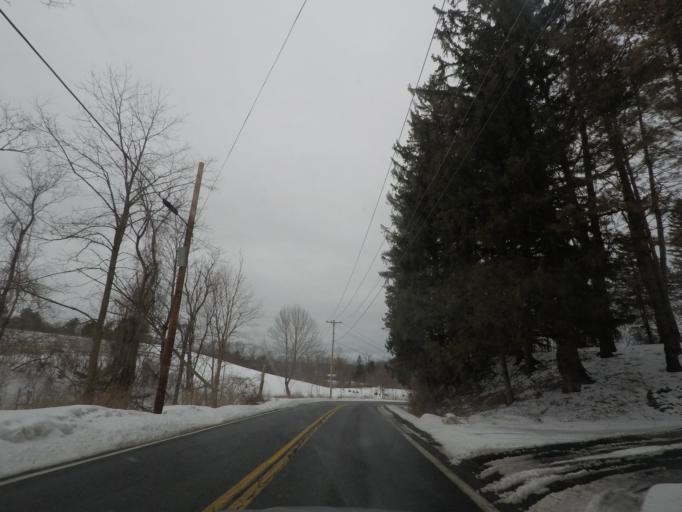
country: US
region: New York
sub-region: Schenectady County
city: Niskayuna
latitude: 42.7687
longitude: -73.8062
